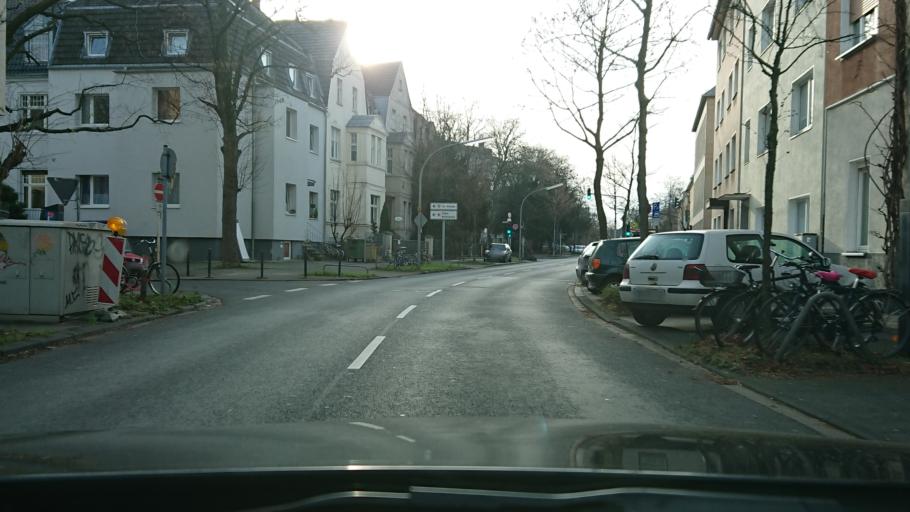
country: DE
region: North Rhine-Westphalia
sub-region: Regierungsbezirk Koln
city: Neustadt/Sued
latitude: 50.9285
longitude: 6.9192
